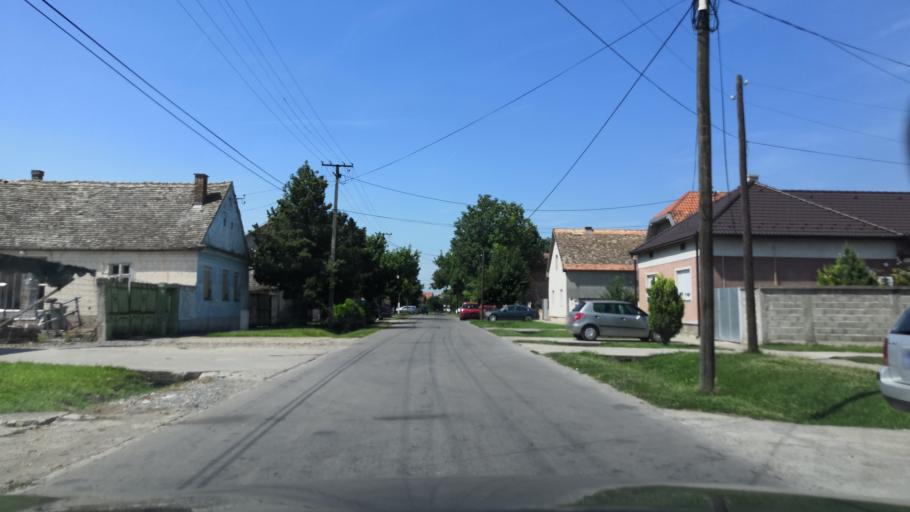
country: RS
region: Autonomna Pokrajina Vojvodina
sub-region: Sremski Okrug
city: Stara Pazova
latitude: 44.9932
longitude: 20.1506
